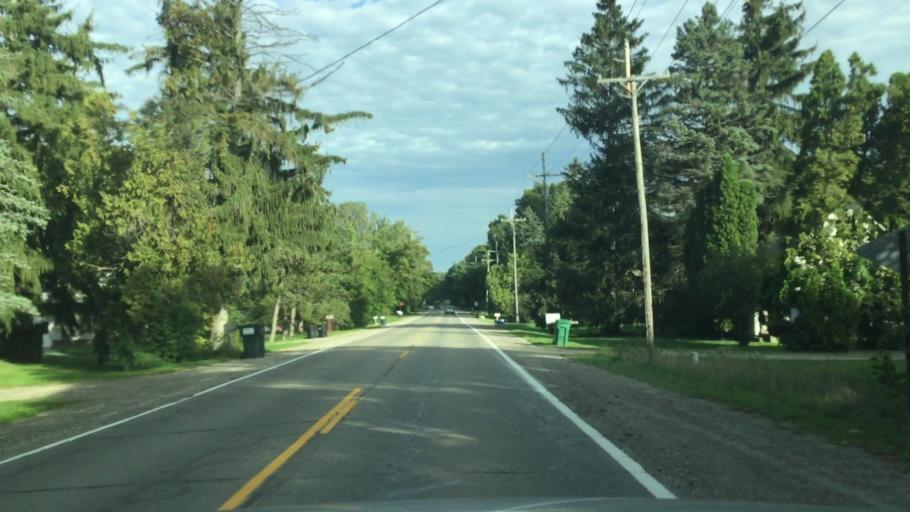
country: US
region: Michigan
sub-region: Livingston County
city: Brighton
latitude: 42.5223
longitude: -83.8573
